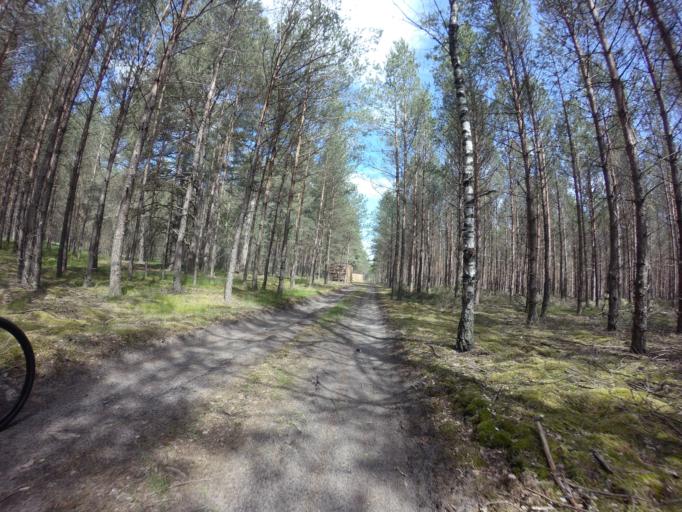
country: PL
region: West Pomeranian Voivodeship
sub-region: Powiat drawski
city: Kalisz Pomorski
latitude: 53.1831
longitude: 15.9648
